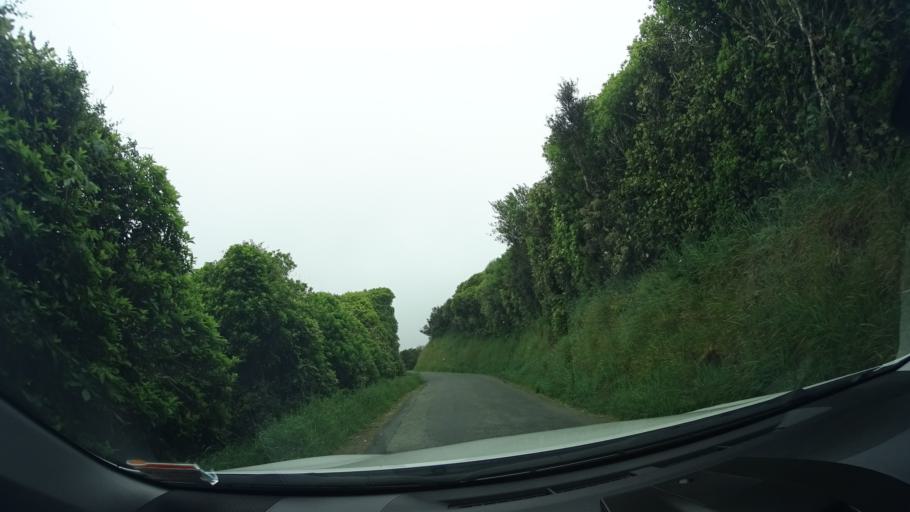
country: NZ
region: Wellington
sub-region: Wellington City
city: Brooklyn
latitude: -41.3062
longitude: 174.7477
